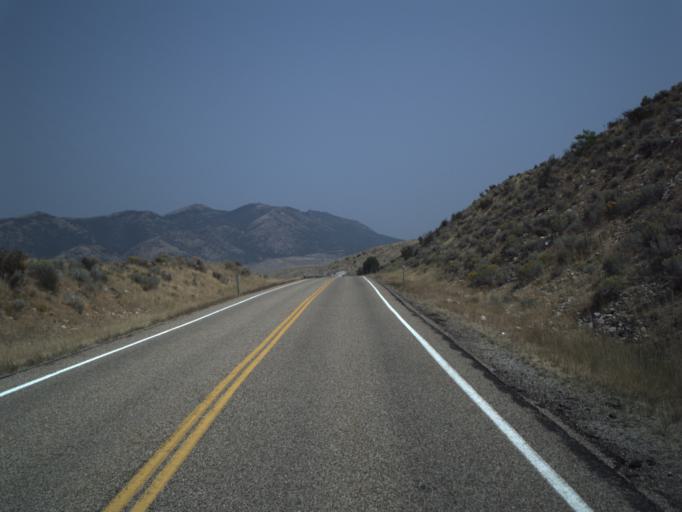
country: US
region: Utah
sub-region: Summit County
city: Summit Park
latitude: 40.9006
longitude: -111.5884
